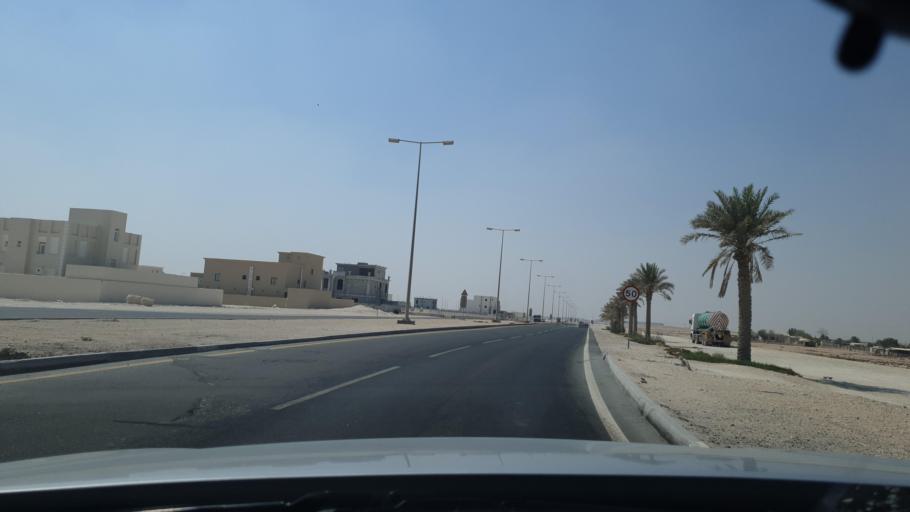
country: QA
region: Al Khawr
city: Al Khawr
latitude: 25.6767
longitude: 51.4755
